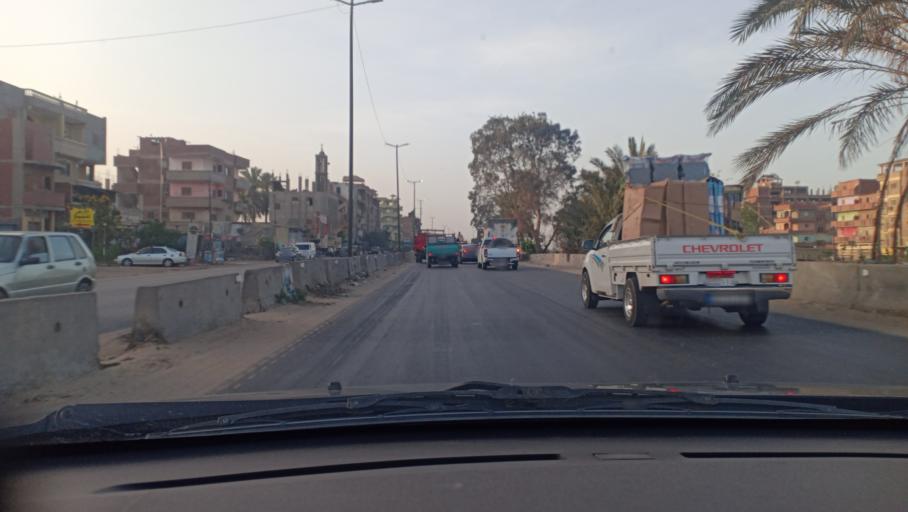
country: EG
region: Muhafazat al Minufiyah
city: Quwaysina
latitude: 30.5769
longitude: 31.2735
